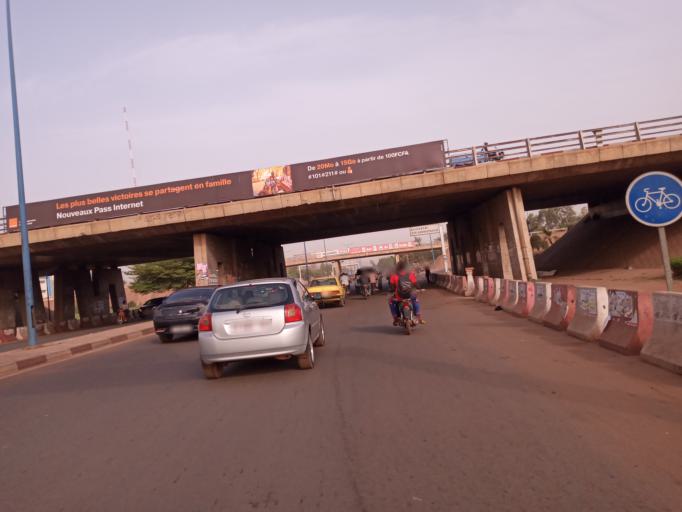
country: ML
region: Bamako
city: Bamako
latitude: 12.6317
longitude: -8.0109
